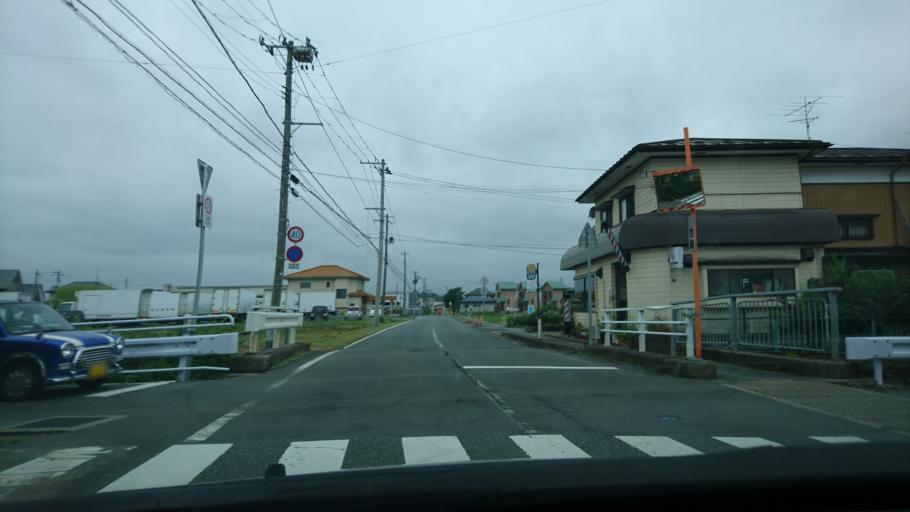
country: JP
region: Iwate
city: Ichinoseki
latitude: 38.9379
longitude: 141.0923
